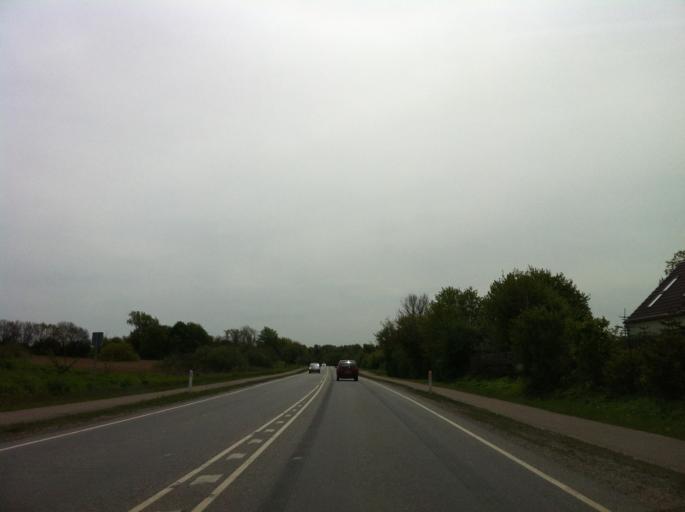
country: DK
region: Zealand
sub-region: Roskilde Kommune
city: Jyllinge
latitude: 55.7153
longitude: 12.1122
